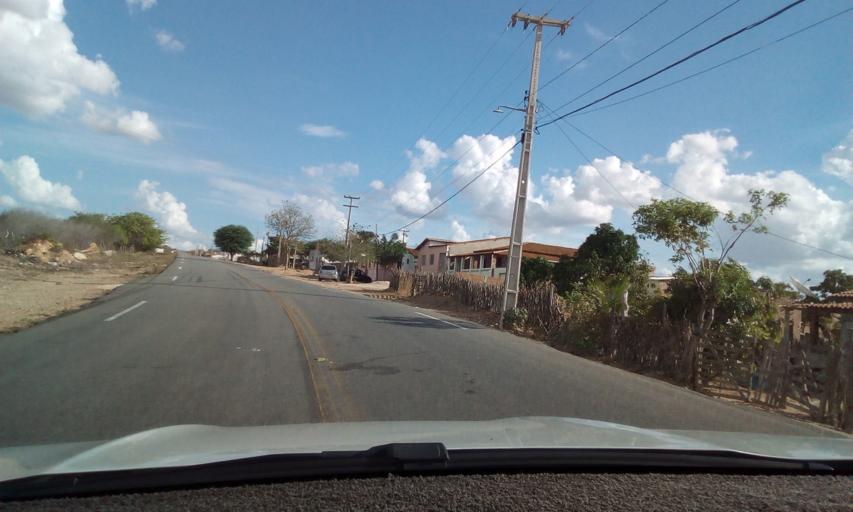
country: BR
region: Paraiba
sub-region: Soledade
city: Soledade
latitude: -6.8584
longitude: -36.4080
